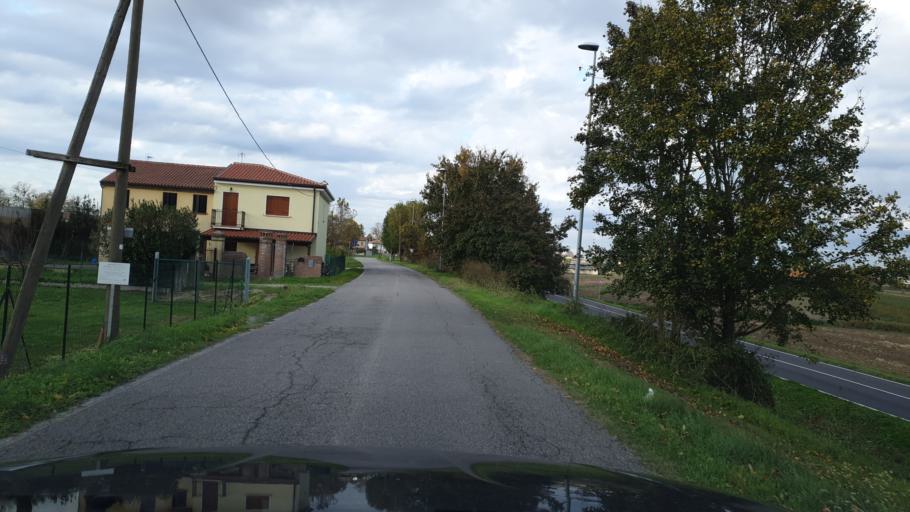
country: IT
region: Veneto
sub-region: Provincia di Rovigo
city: Villanova del Ghebbo Canton
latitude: 45.0449
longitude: 11.6481
